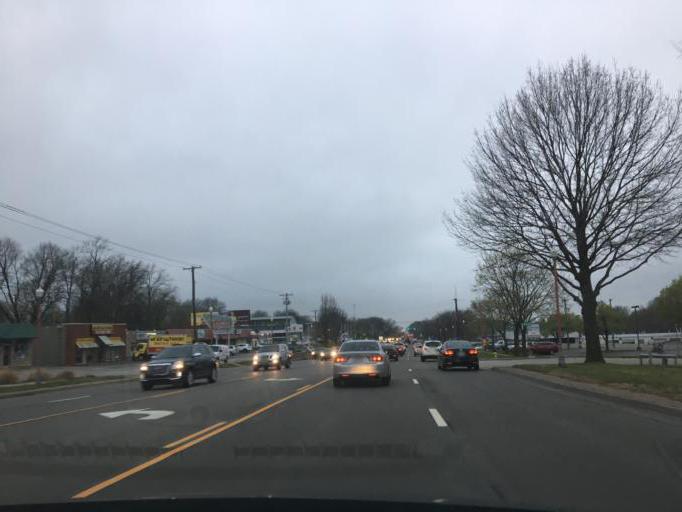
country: US
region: Kansas
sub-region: Johnson County
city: Merriam
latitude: 39.0150
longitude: -94.6748
